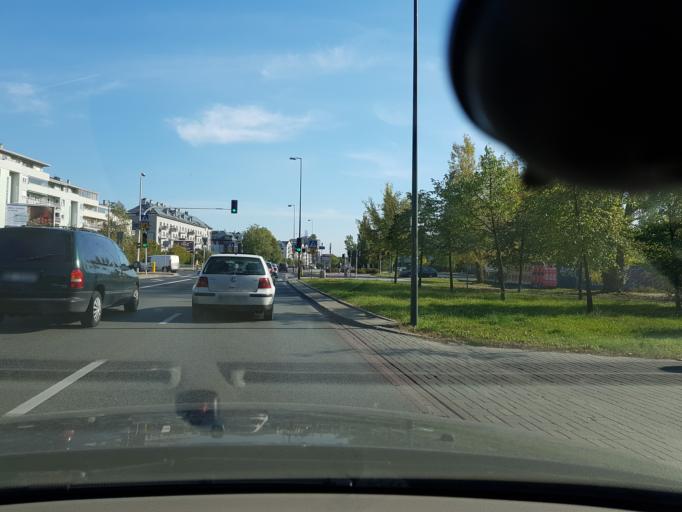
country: PL
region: Masovian Voivodeship
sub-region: Warszawa
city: Ursynow
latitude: 52.1531
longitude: 21.0552
